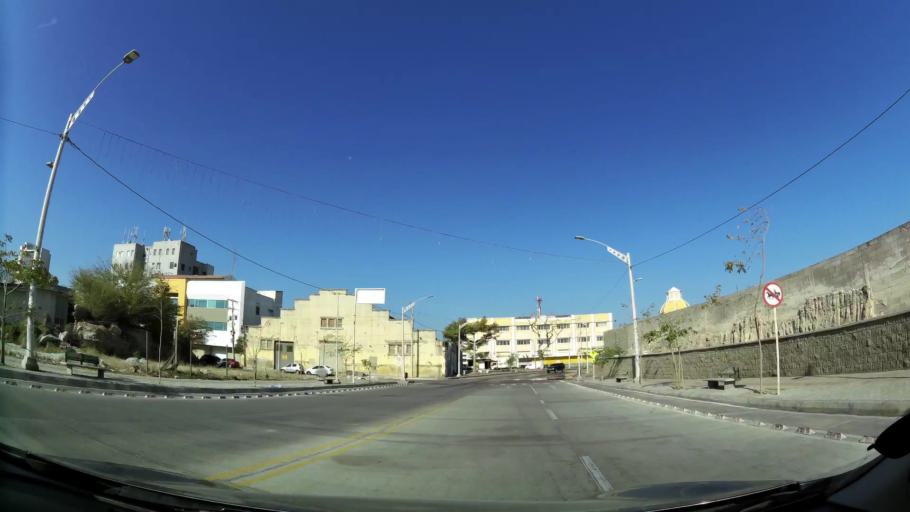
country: CO
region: Atlantico
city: Barranquilla
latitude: 10.9877
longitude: -74.7782
